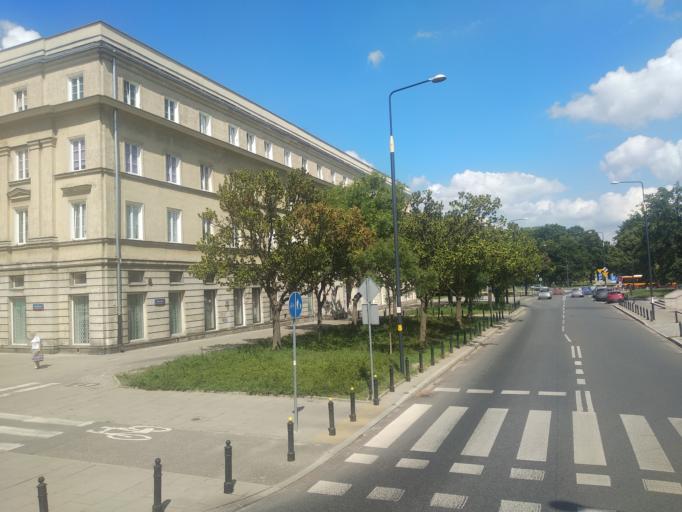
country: PL
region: Masovian Voivodeship
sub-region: Warszawa
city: Wola
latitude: 52.2468
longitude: 20.9974
